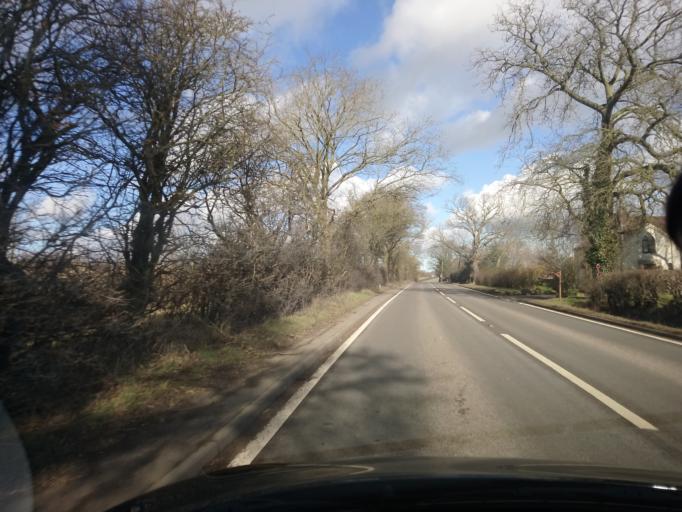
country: GB
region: England
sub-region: Shropshire
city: Astley
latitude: 52.7622
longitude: -2.7165
